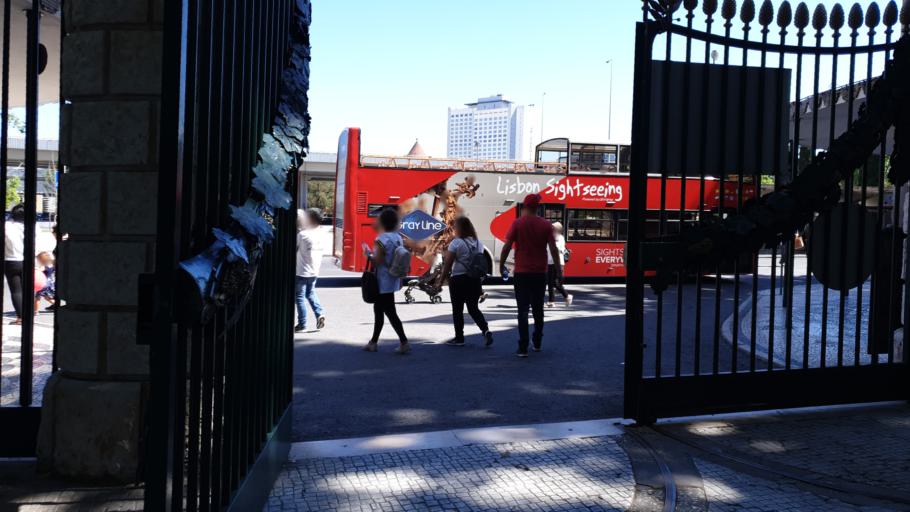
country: PT
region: Lisbon
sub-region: Odivelas
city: Pontinha
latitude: 38.7430
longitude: -9.1683
